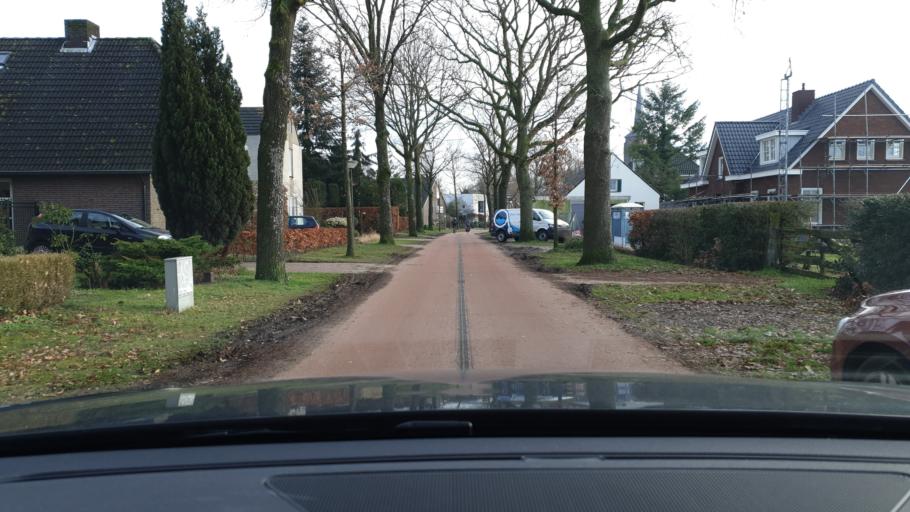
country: NL
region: North Brabant
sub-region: Gemeente Geldrop-Mierlo
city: Geldrop
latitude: 51.4200
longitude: 5.5389
